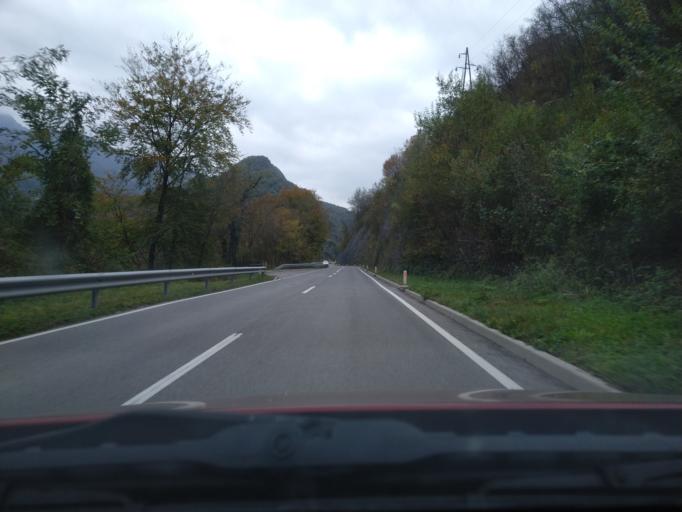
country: SI
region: Kobarid
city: Kobarid
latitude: 46.2655
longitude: 13.5749
